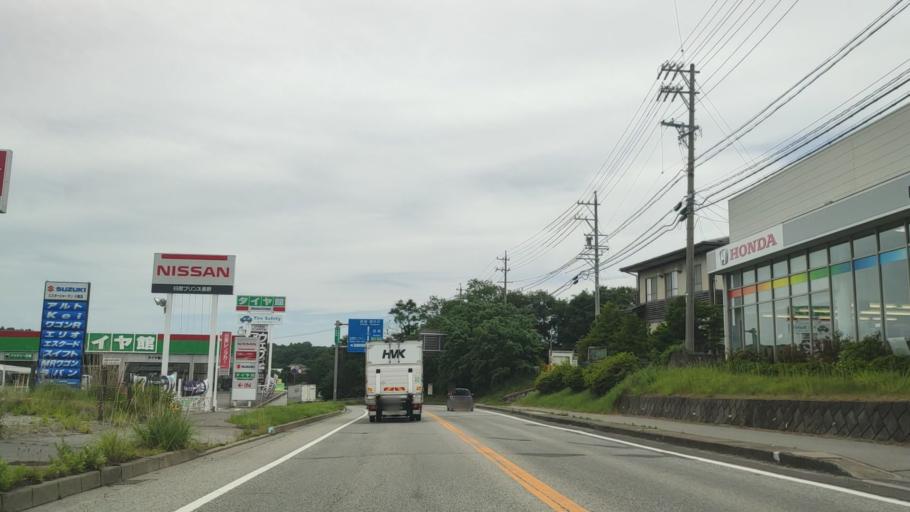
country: JP
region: Nagano
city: Komoro
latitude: 36.3132
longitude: 138.4535
